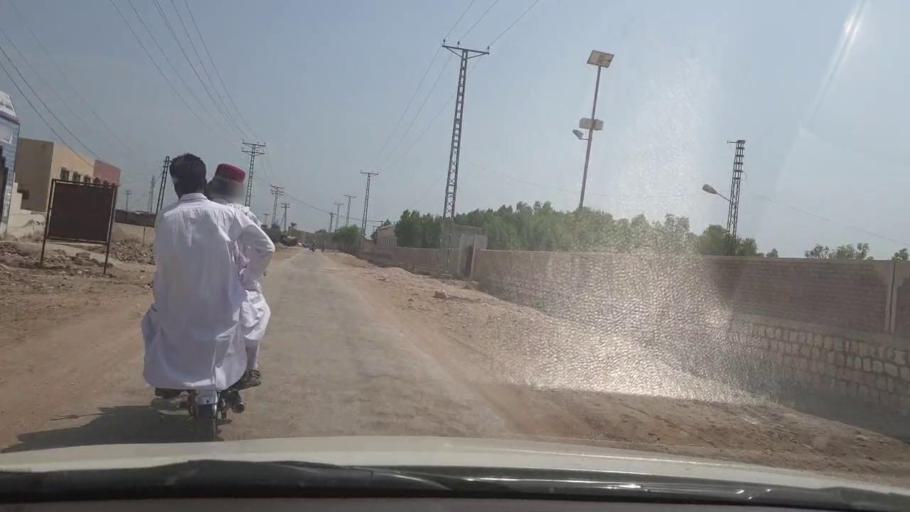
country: PK
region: Sindh
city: Garhi Yasin
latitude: 27.9128
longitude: 68.5110
